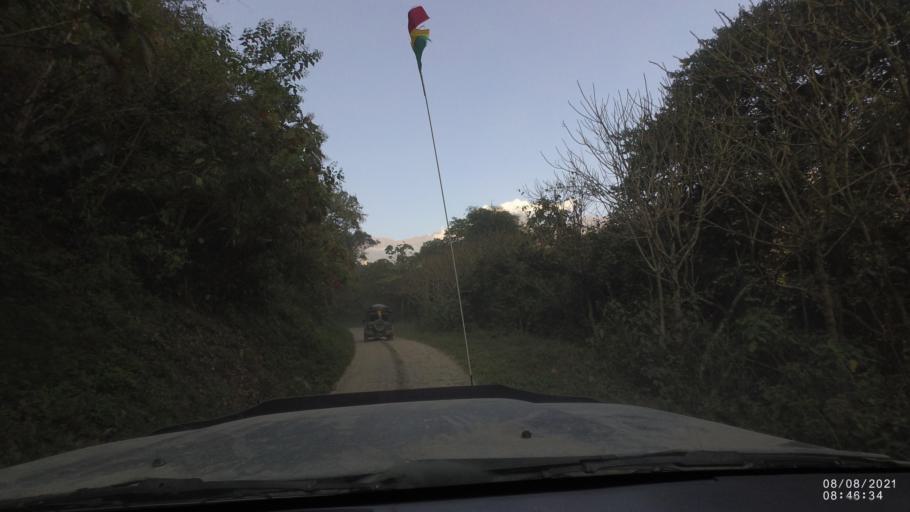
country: BO
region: La Paz
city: Quime
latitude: -16.5260
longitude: -66.7521
